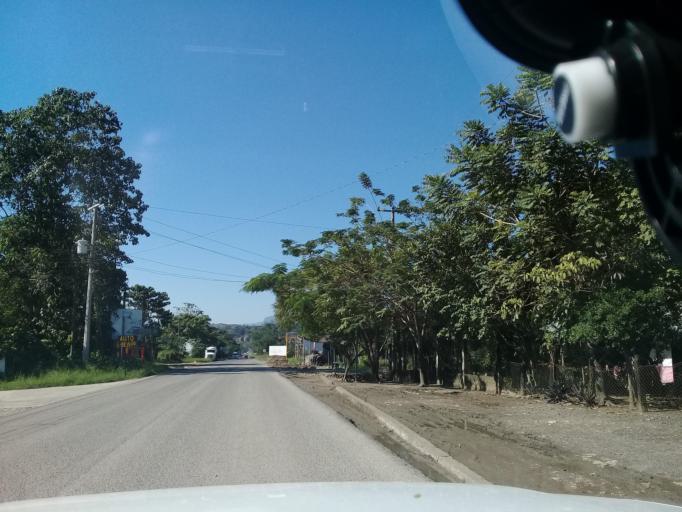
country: MX
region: Hidalgo
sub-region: Huejutla de Reyes
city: Parque de Poblamiento Solidaridad
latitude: 21.1604
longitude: -98.4064
